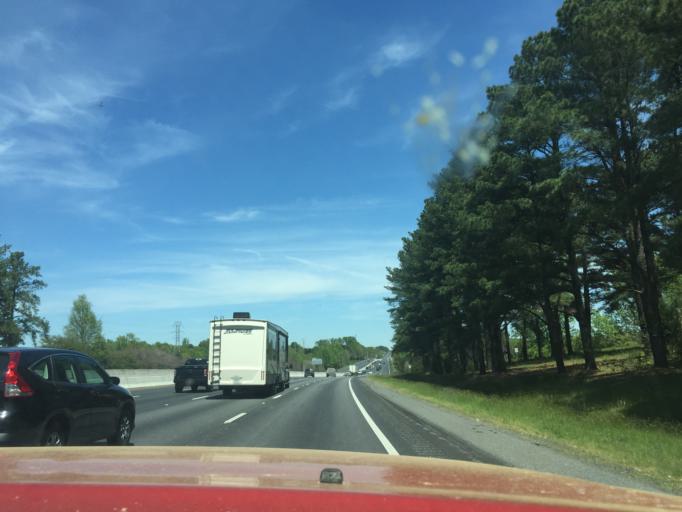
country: US
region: South Carolina
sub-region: York County
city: Fort Mill
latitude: 35.0613
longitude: -80.9559
